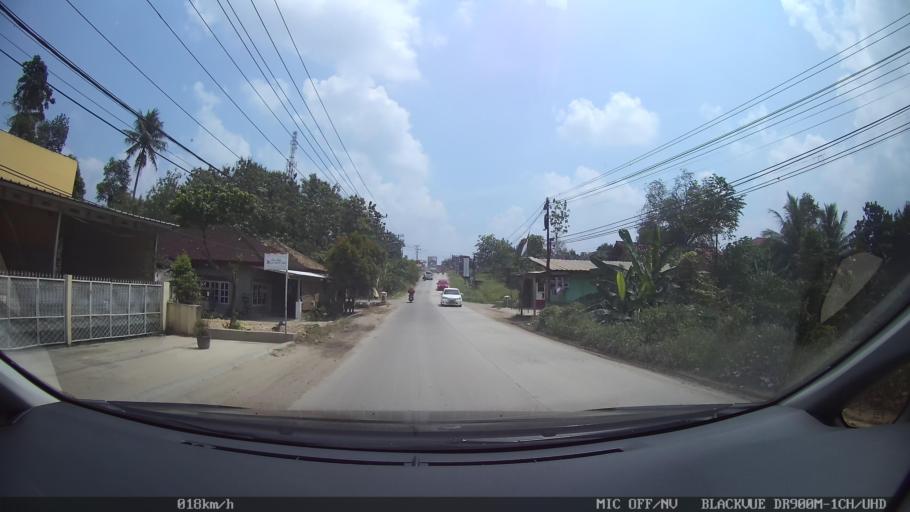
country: ID
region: Lampung
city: Pringsewu
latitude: -5.3397
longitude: 104.9752
